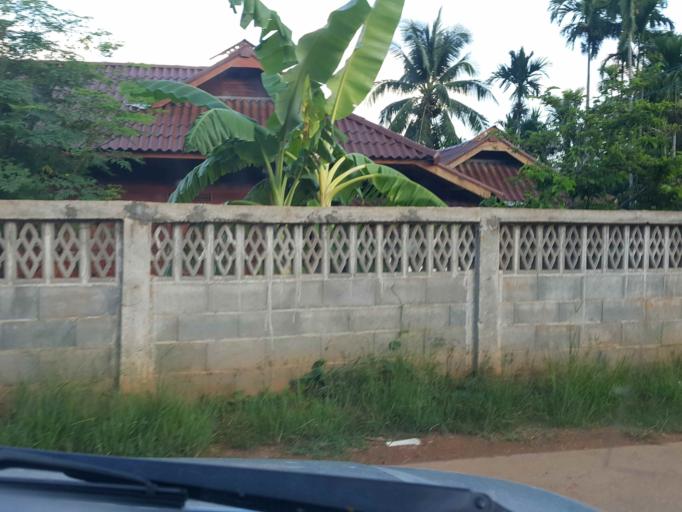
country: TH
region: Chiang Mai
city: Mae Chaem
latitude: 18.4902
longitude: 98.3867
